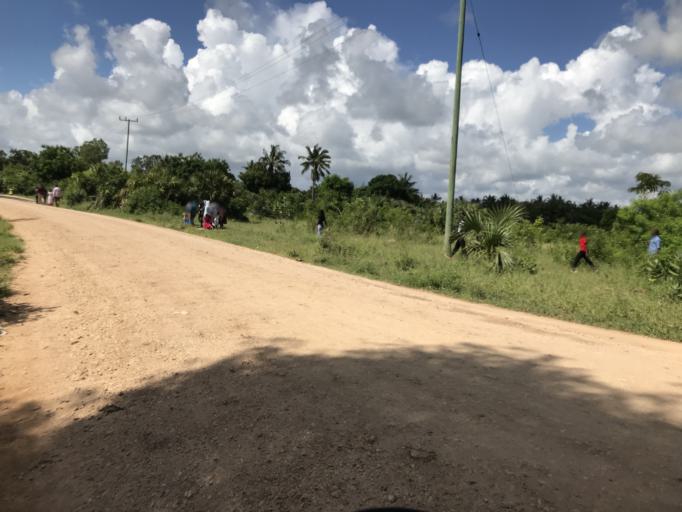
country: TZ
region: Dar es Salaam
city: Dar es Salaam
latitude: -6.8836
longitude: 39.4378
